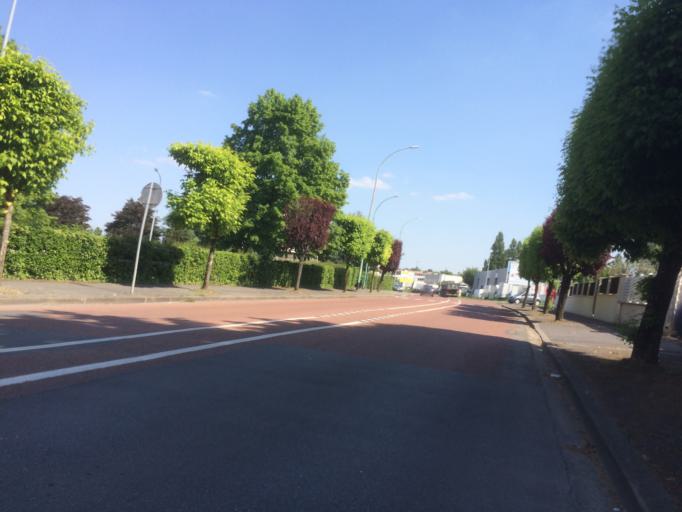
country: FR
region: Ile-de-France
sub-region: Departement de l'Essonne
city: Morangis
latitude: 48.6963
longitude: 2.3338
